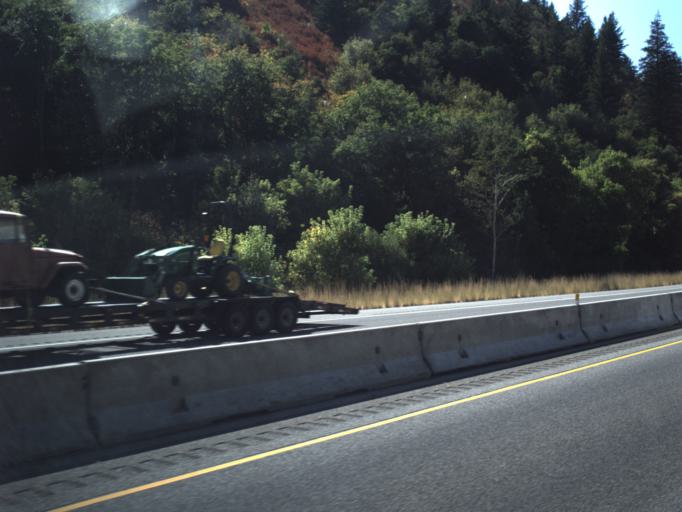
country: US
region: Utah
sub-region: Cache County
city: Wellsville
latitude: 41.6045
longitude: -111.9660
